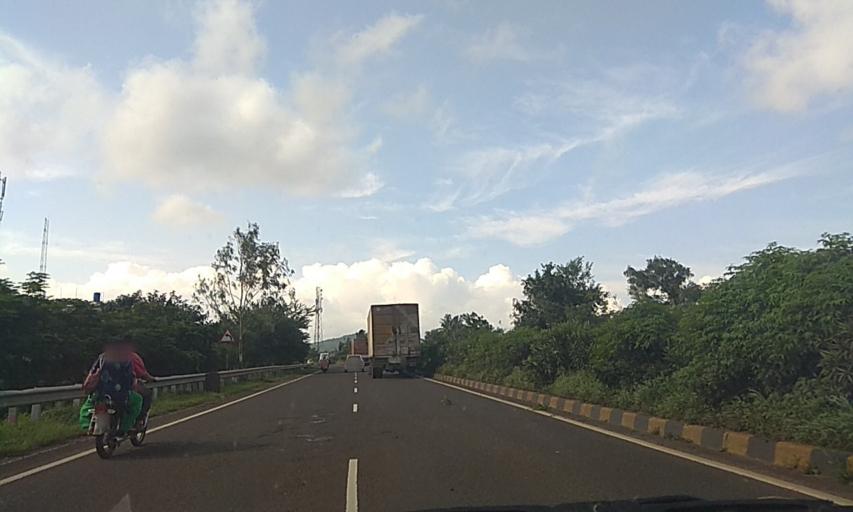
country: IN
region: Maharashtra
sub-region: Kolhapur
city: Kodoli
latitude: 16.9250
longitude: 74.2890
